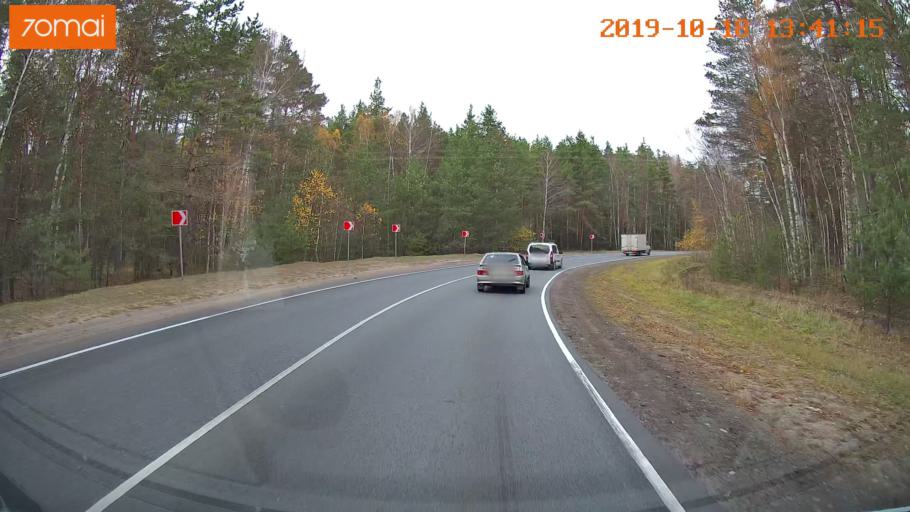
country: RU
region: Rjazan
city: Solotcha
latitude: 54.9188
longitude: 39.9965
